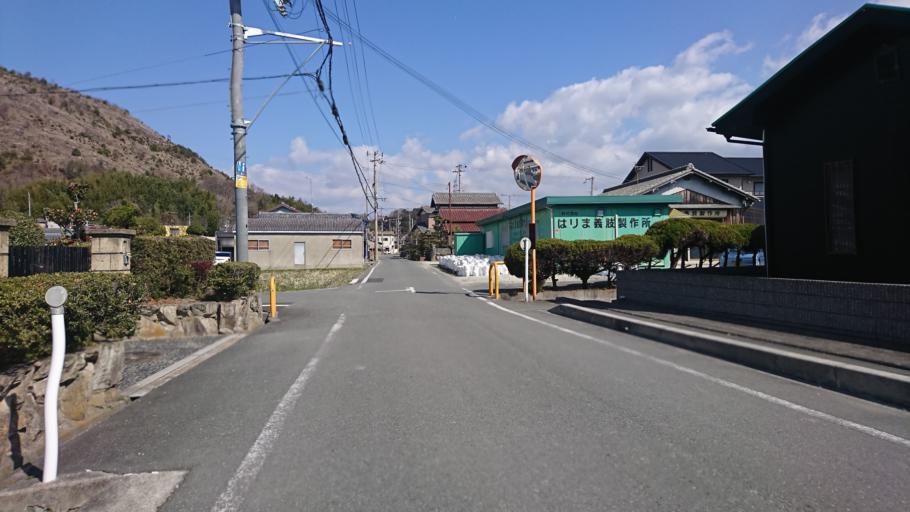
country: JP
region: Hyogo
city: Kakogawacho-honmachi
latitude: 34.7962
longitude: 134.8076
